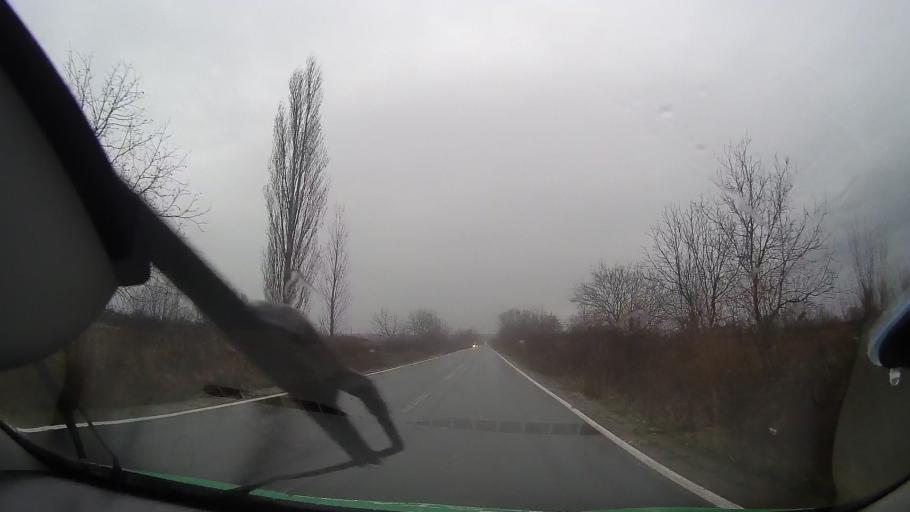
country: RO
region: Bihor
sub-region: Comuna Tinca
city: Tinca
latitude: 46.7556
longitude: 21.9362
